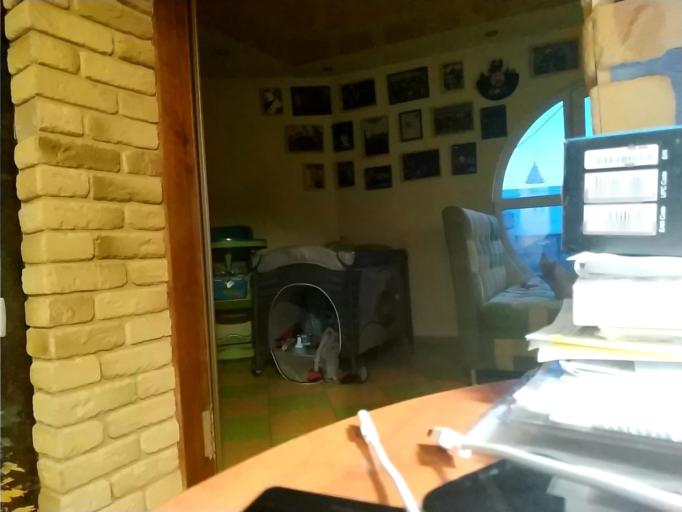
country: RU
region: Republic of Karelia
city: Belomorsk
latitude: 64.4449
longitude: 34.6345
